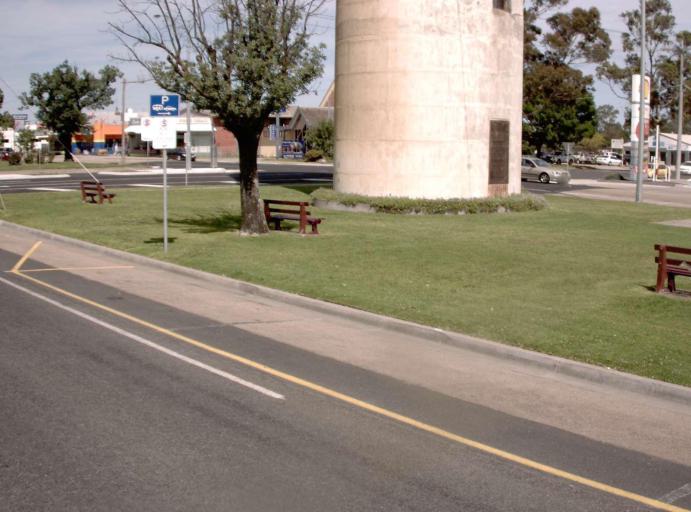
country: AU
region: Victoria
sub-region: East Gippsland
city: Bairnsdale
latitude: -37.8268
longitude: 147.6263
